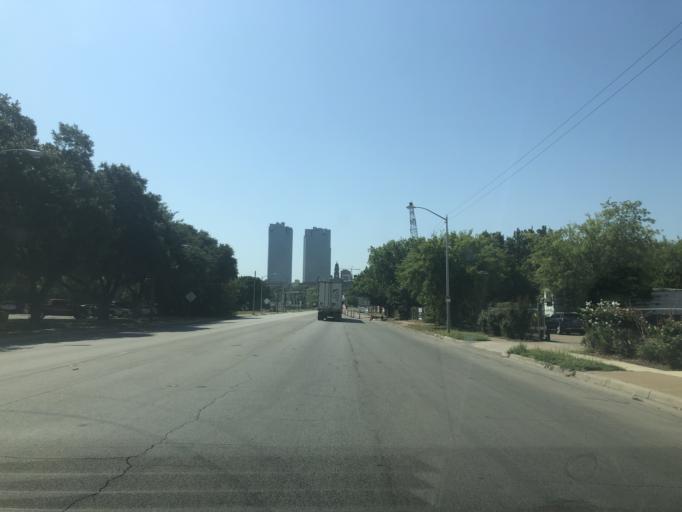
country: US
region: Texas
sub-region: Tarrant County
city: Fort Worth
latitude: 32.7652
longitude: -97.3385
